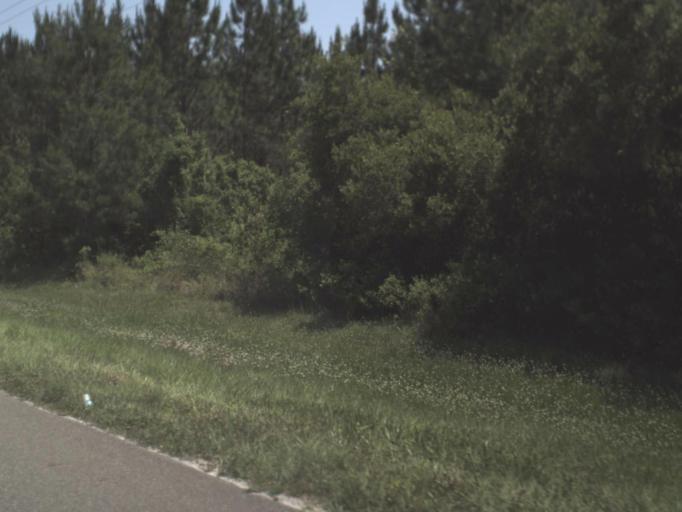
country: US
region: Florida
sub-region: Bradford County
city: Starke
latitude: 29.9050
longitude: -82.0904
